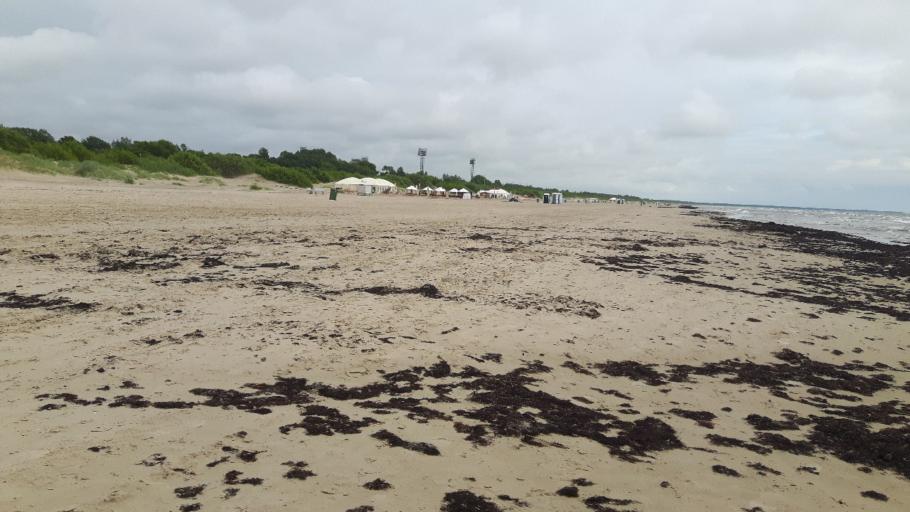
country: LV
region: Liepaja
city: Liepaja
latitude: 56.5086
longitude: 20.9888
